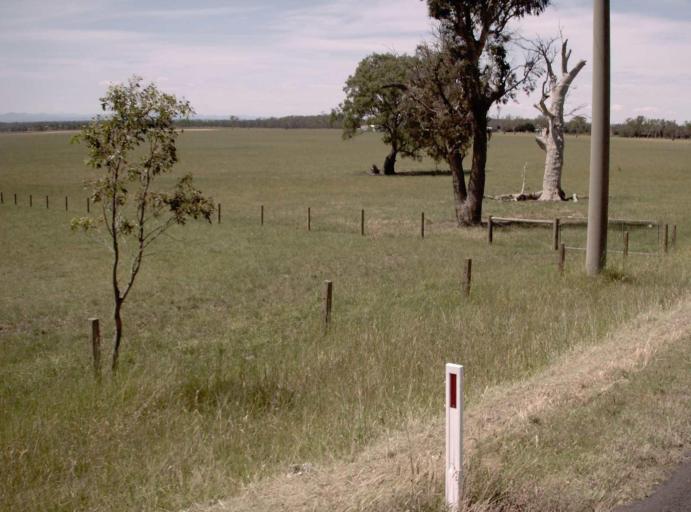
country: AU
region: Victoria
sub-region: Latrobe
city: Traralgon
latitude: -38.1756
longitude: 146.6482
